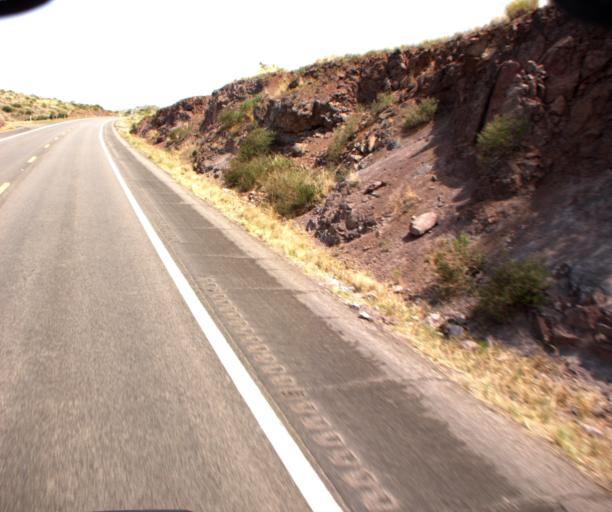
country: US
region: Arizona
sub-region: Greenlee County
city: Clifton
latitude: 32.7671
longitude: -109.2555
